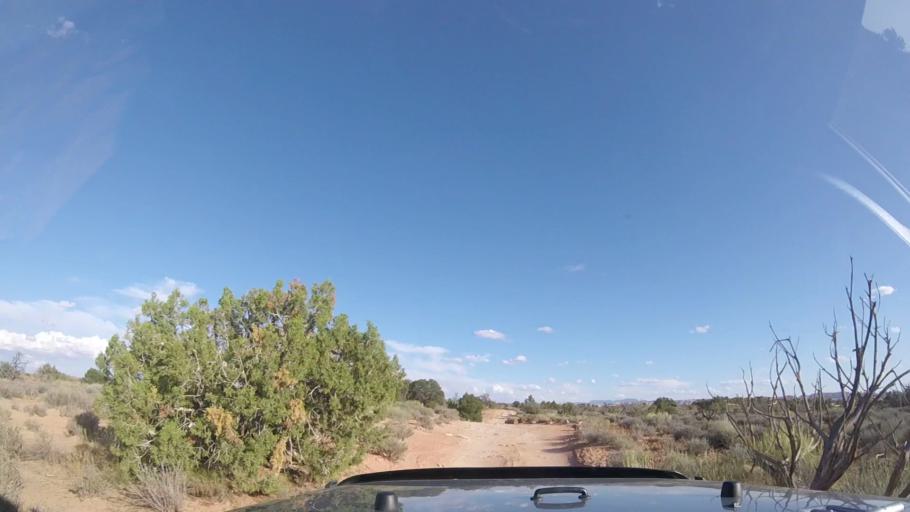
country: US
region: Utah
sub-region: Grand County
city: Moab
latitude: 38.2140
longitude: -109.8116
